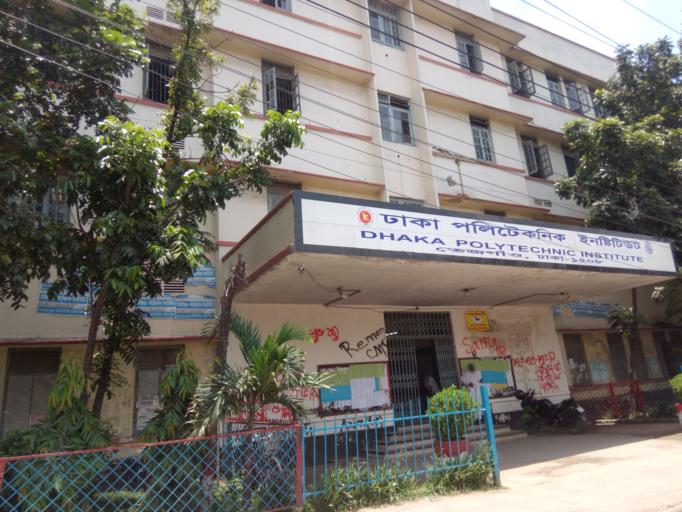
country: BD
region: Dhaka
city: Paltan
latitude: 23.7592
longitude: 90.3995
